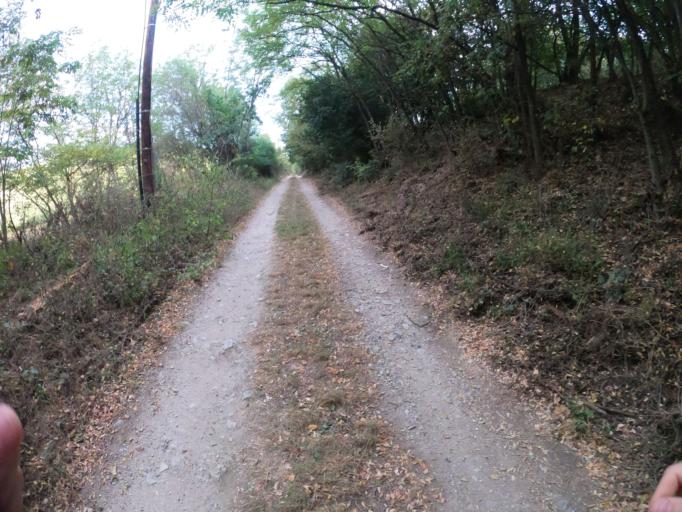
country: HU
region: Veszprem
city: Revfueloep
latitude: 46.8913
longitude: 17.5598
